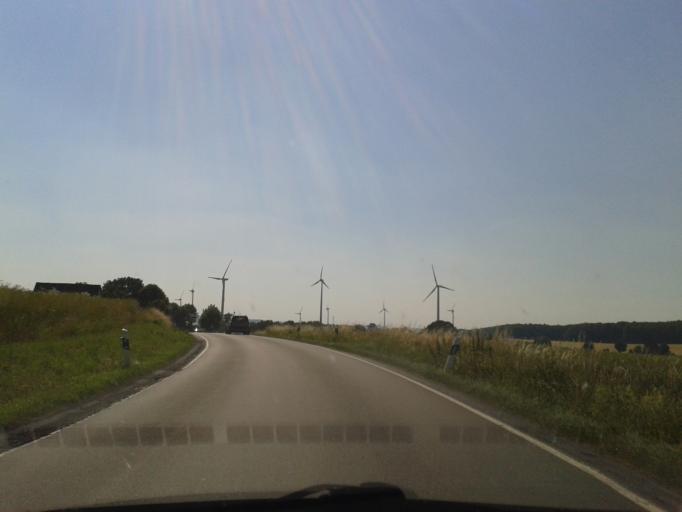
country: DE
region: North Rhine-Westphalia
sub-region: Regierungsbezirk Detmold
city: Blomberg
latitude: 51.9798
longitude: 9.0641
